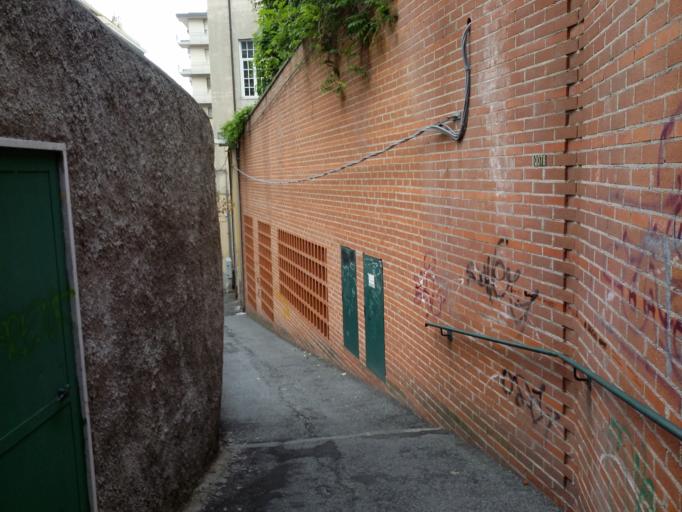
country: IT
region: Liguria
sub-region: Provincia di Genova
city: San Teodoro
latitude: 44.4123
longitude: 8.8934
